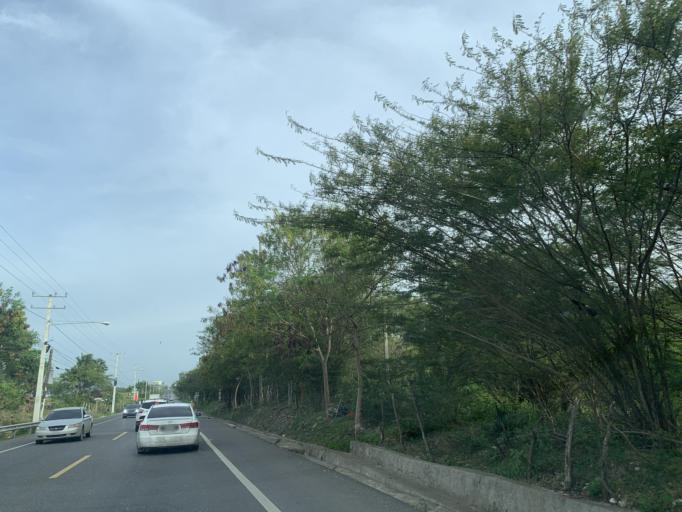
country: DO
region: Puerto Plata
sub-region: Puerto Plata
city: Puerto Plata
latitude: 19.7414
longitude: -70.6338
